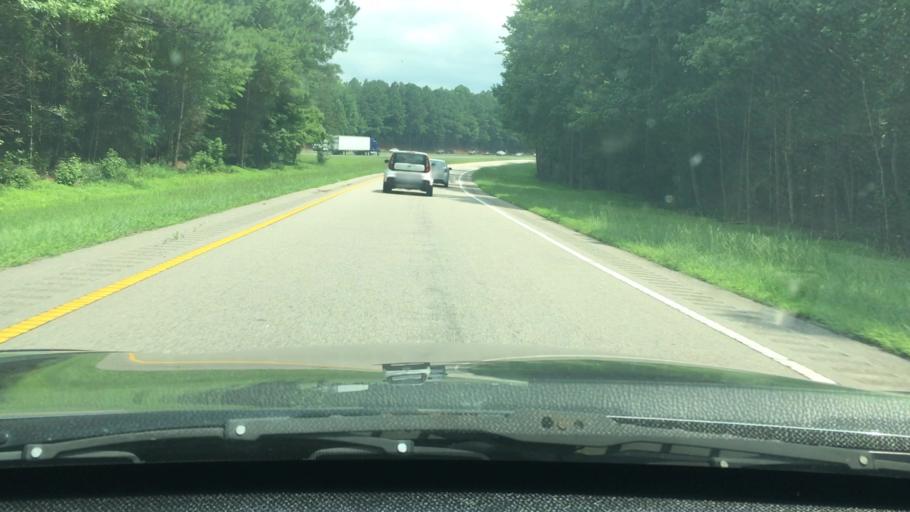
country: US
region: North Carolina
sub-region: Wake County
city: Cary
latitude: 35.8108
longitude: -78.7397
